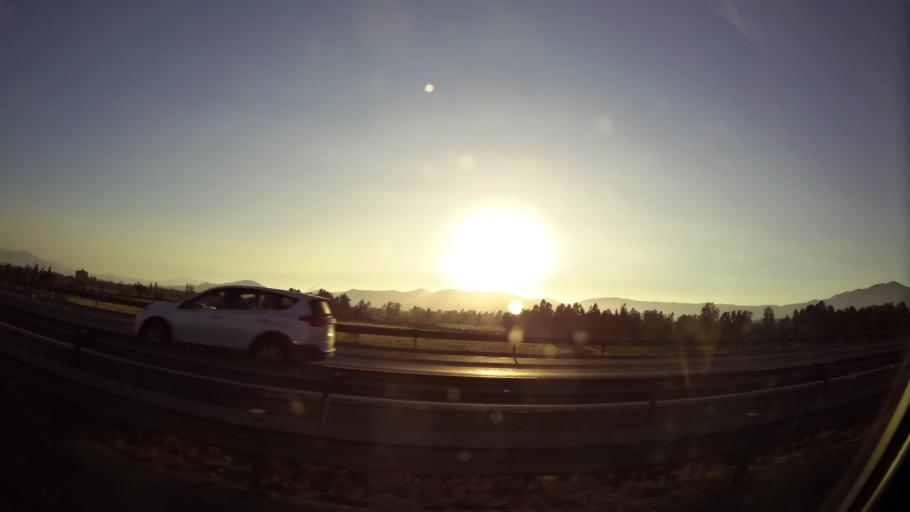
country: CL
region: Santiago Metropolitan
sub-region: Provincia de Talagante
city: Penaflor
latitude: -33.5921
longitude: -70.8445
